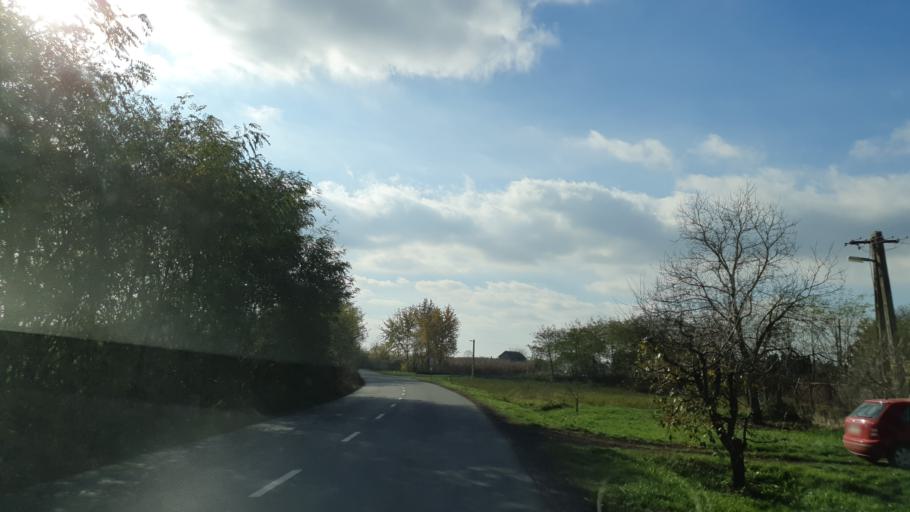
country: HU
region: Szabolcs-Szatmar-Bereg
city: Nyirkarasz
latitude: 48.0906
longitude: 22.0938
